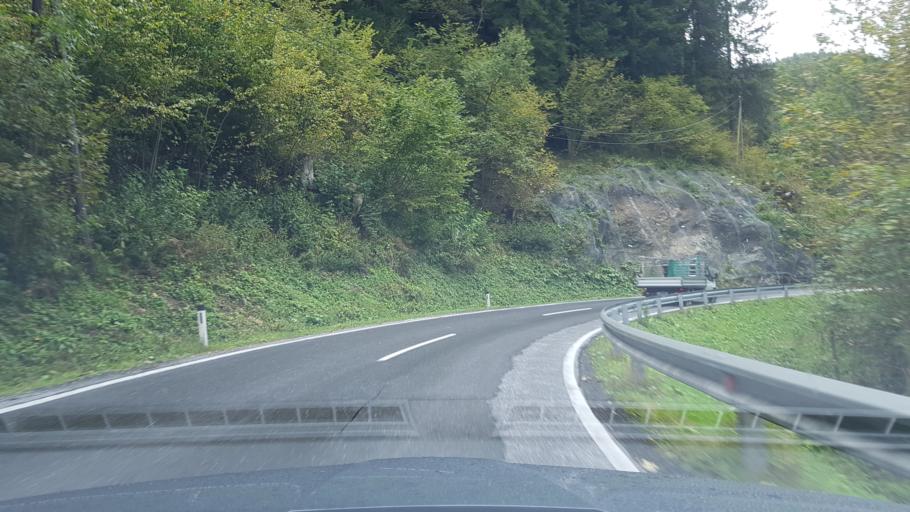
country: AT
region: Styria
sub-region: Politischer Bezirk Voitsberg
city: Salla
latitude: 47.1106
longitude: 15.0108
